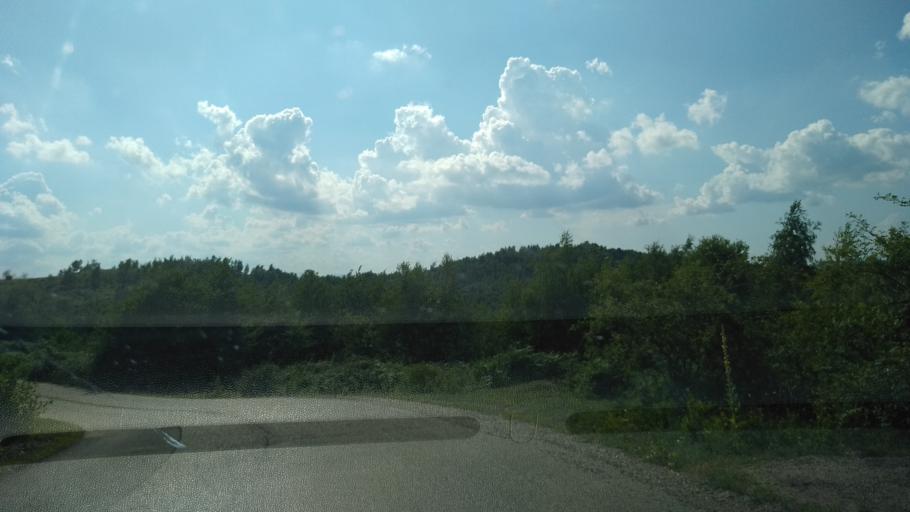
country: RO
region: Hunedoara
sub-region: Comuna Orastioara de Sus
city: Orastioara de Sus
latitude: 45.7117
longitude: 23.1526
